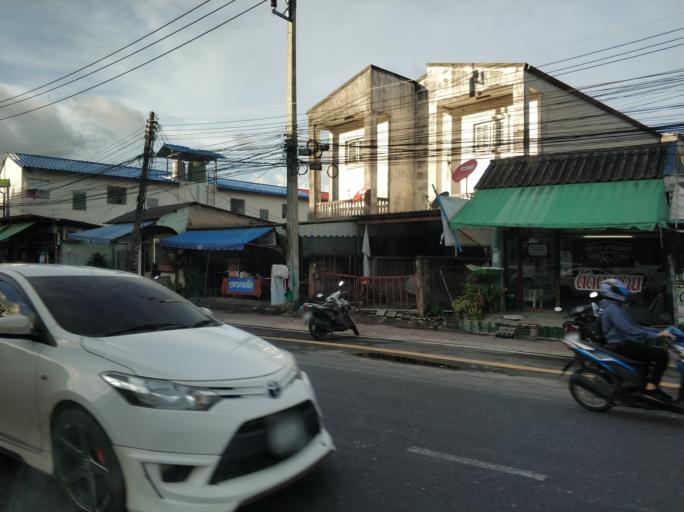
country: TH
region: Phuket
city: Kathu
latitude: 7.9084
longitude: 98.3356
